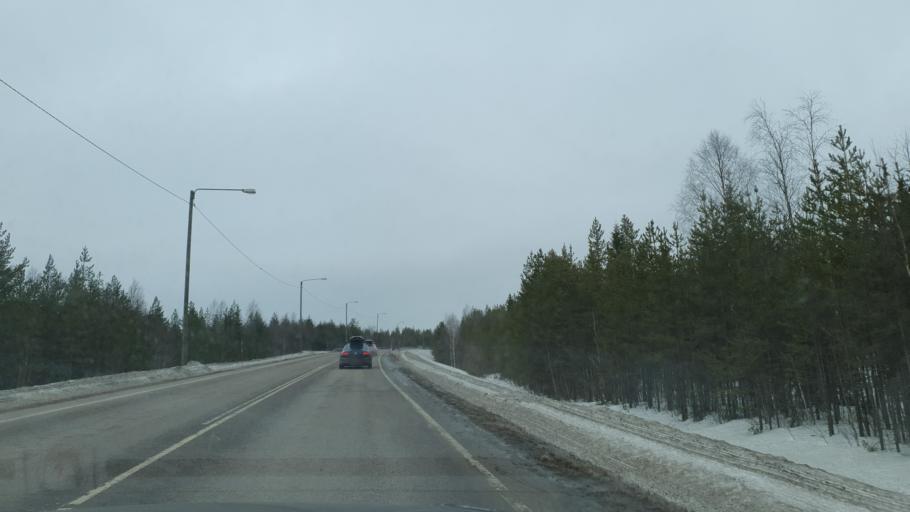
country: FI
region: Lapland
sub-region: Torniolaakso
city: Pello
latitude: 66.8285
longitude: 24.0012
